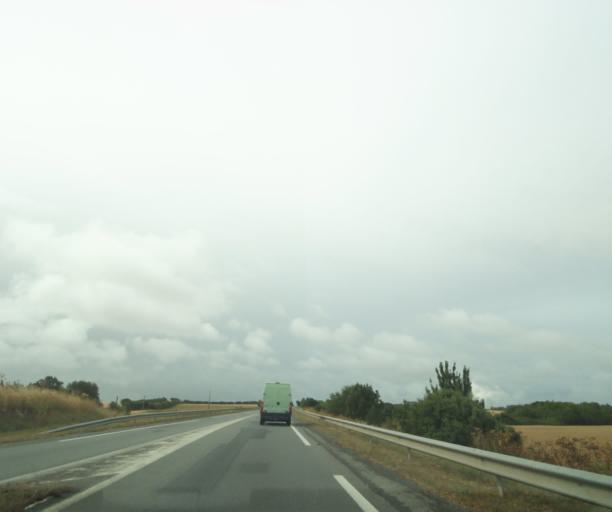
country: FR
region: Poitou-Charentes
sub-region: Departement de la Charente-Maritime
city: Marsilly
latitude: 46.2076
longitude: -1.1369
